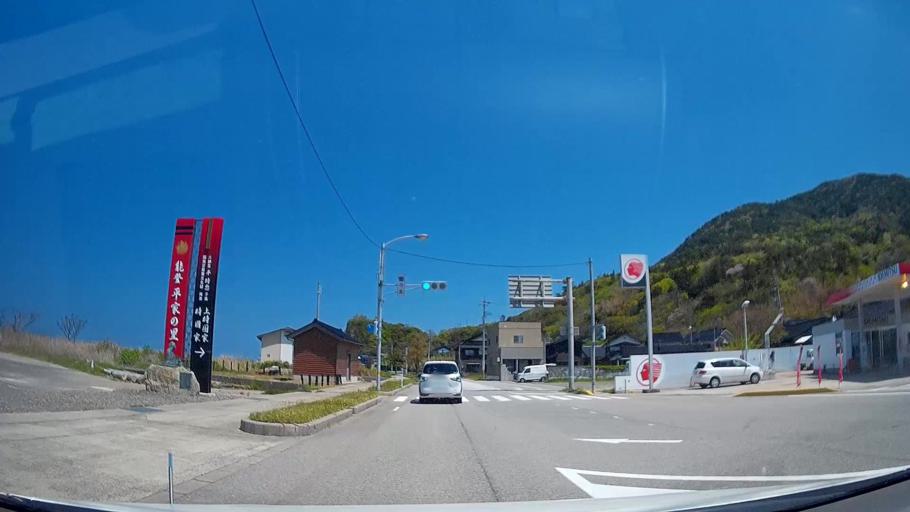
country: JP
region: Ishikawa
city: Nanao
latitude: 37.4530
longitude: 137.0729
